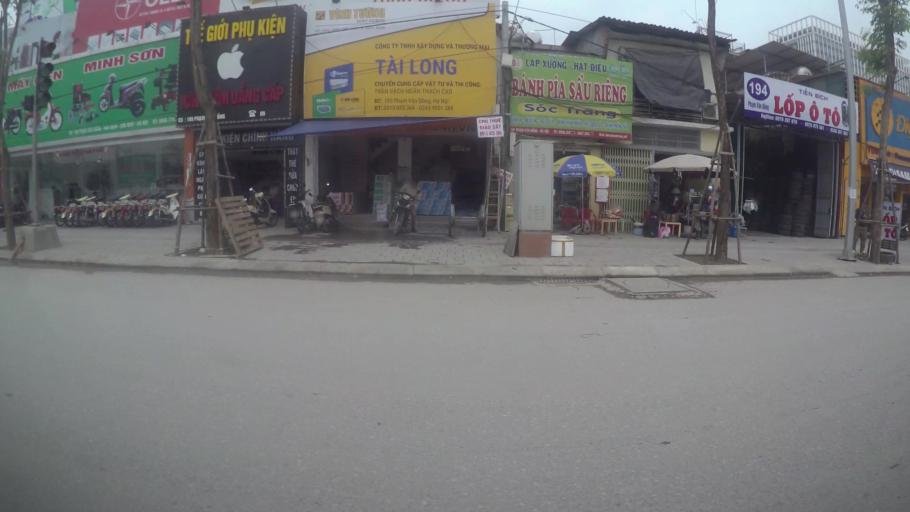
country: VN
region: Ha Noi
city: Cau Dien
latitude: 21.0463
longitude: 105.7811
